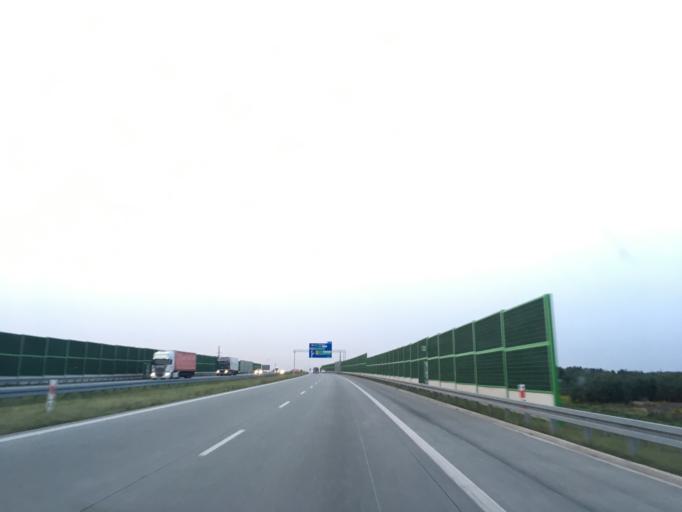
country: PL
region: Lodz Voivodeship
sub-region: Powiat lodzki wschodni
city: Andrespol
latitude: 51.7575
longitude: 19.5951
